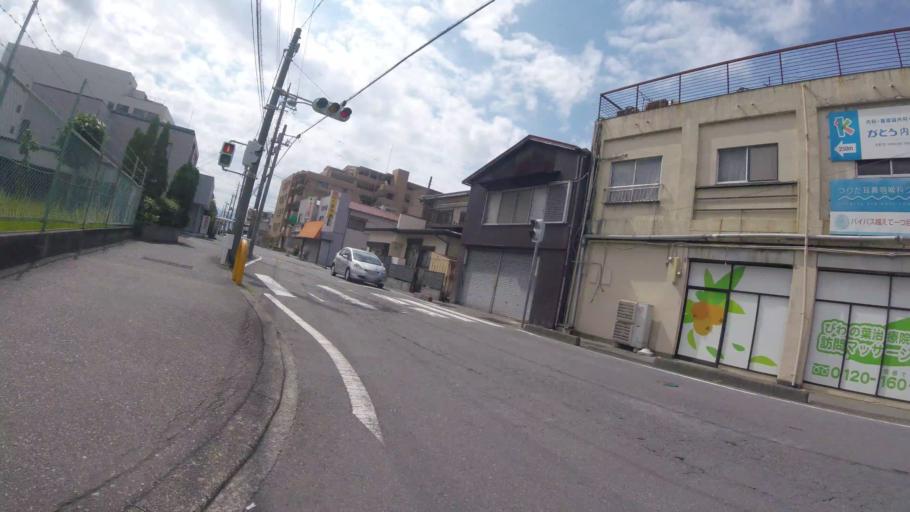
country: JP
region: Shizuoka
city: Numazu
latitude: 35.1163
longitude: 138.8714
